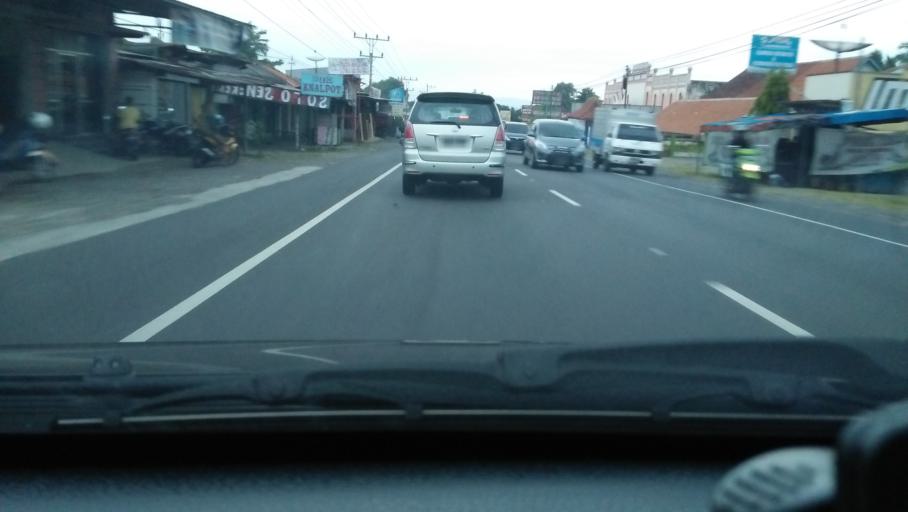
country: ID
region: Central Java
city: Magelang
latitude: -7.4215
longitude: 110.2324
